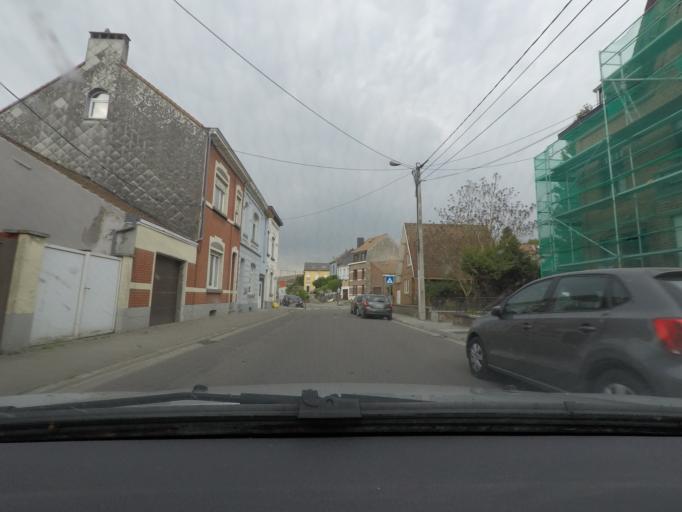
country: BE
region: Wallonia
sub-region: Province du Brabant Wallon
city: Ottignies
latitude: 50.6649
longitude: 4.5707
